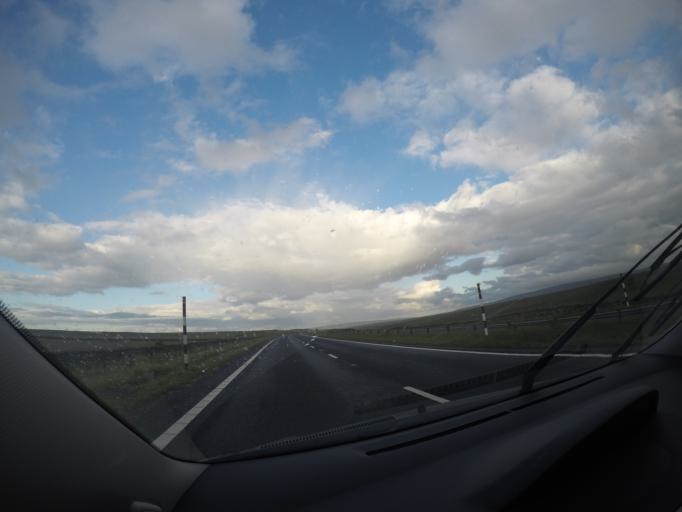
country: GB
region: England
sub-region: County Durham
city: Holwick
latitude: 54.5077
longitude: -2.1695
